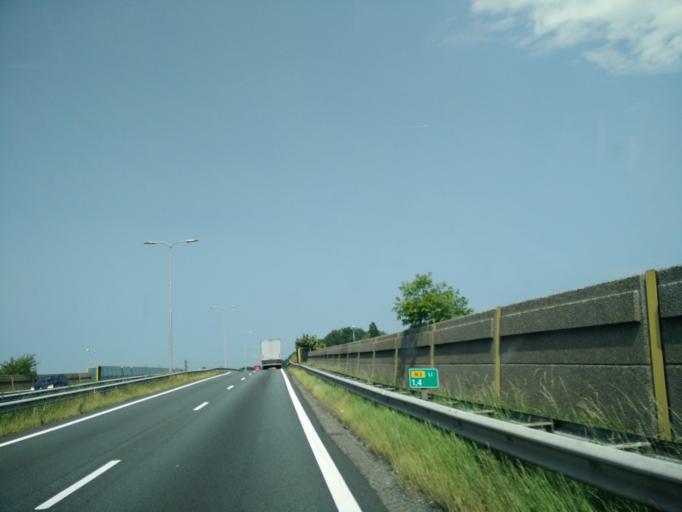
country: NL
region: South Holland
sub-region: Gemeente Papendrecht
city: Papendrecht
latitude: 51.8301
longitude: 4.7060
